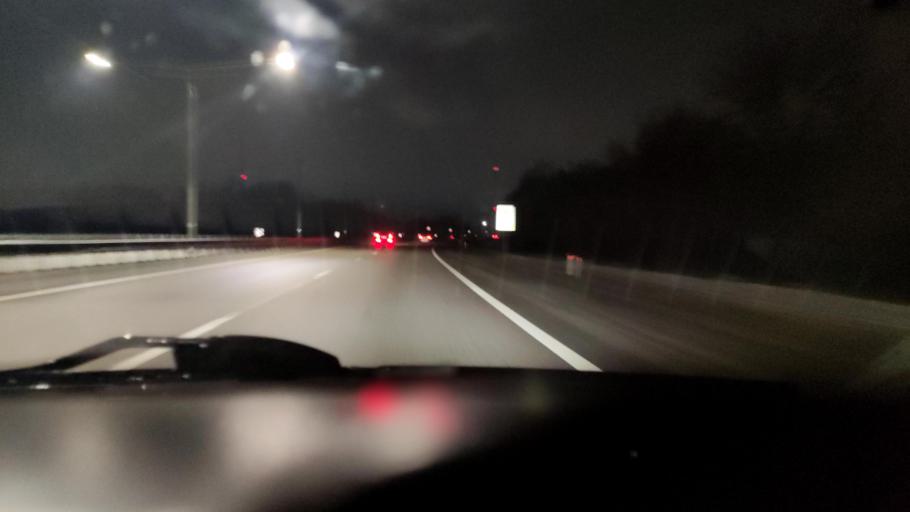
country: RU
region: Voronezj
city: Ramon'
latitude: 51.9983
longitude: 39.2182
